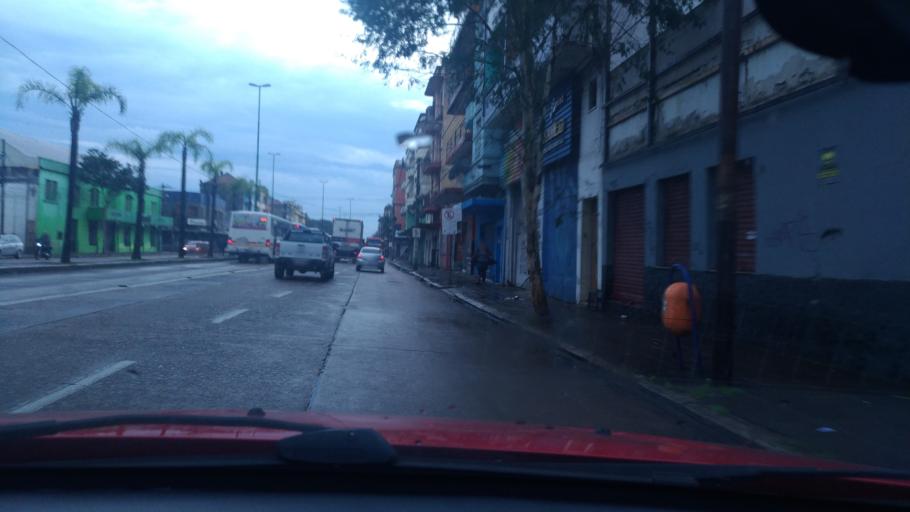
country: BR
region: Rio Grande do Sul
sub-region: Porto Alegre
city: Porto Alegre
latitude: -30.0088
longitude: -51.2019
